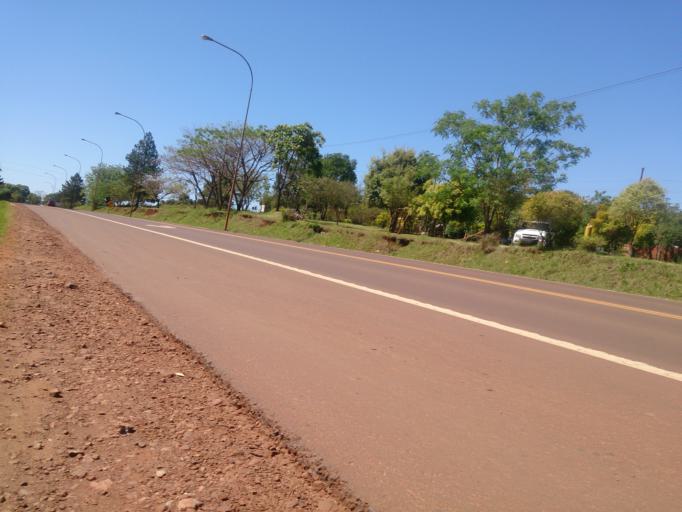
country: AR
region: Misiones
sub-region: Departamento de Obera
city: Obera
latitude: -27.4973
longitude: -55.1066
